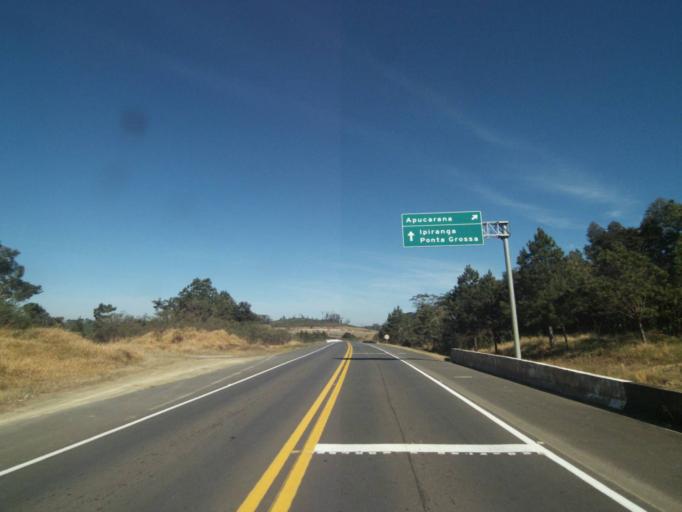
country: BR
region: Parana
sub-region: Tibagi
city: Tibagi
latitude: -24.8111
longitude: -50.4828
